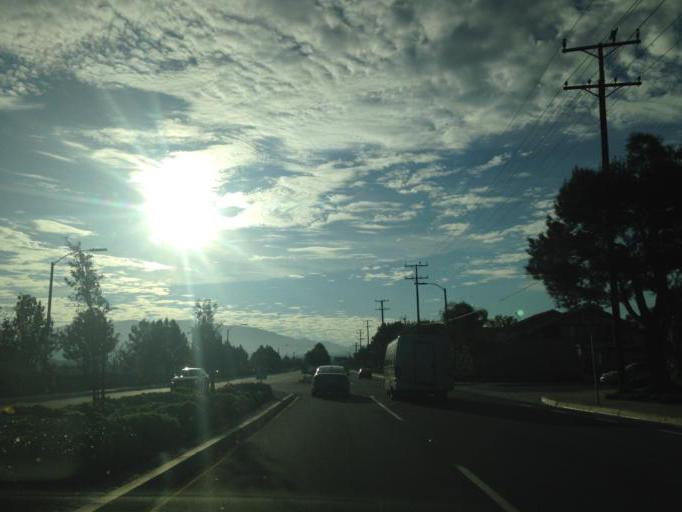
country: US
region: California
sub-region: Riverside County
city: Temecula
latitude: 33.4616
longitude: -117.1105
